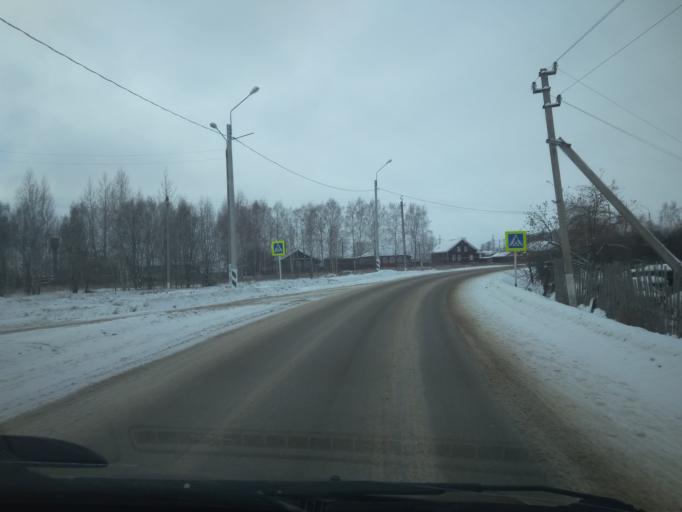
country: RU
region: Mordoviya
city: Ten'gushevo
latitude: 54.7571
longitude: 42.7127
